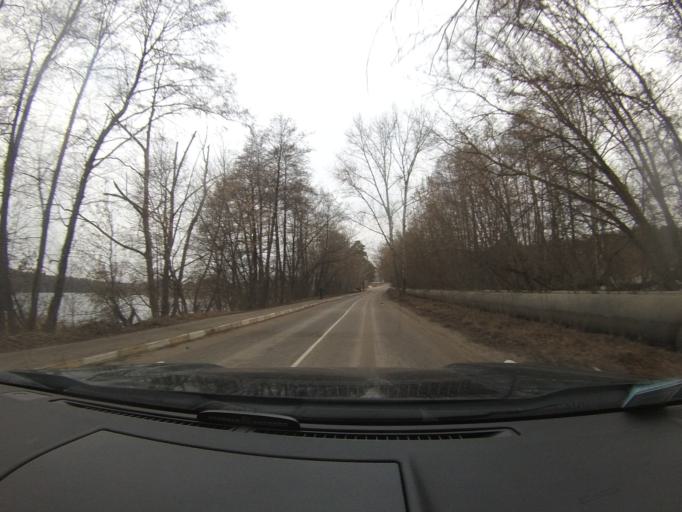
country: RU
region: Moskovskaya
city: Peski
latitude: 55.2637
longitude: 38.7600
